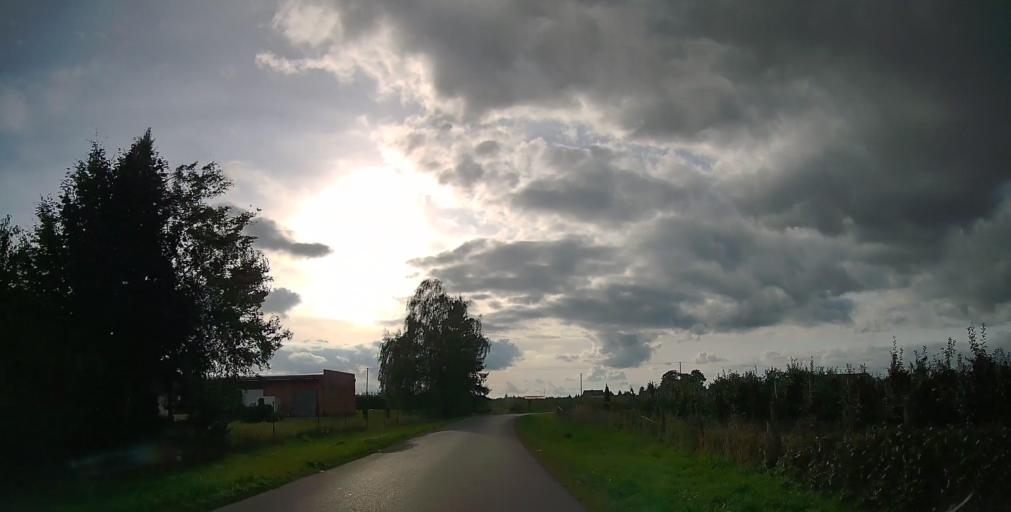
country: PL
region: Masovian Voivodeship
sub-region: Powiat grojecki
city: Jasieniec
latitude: 51.7583
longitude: 20.9468
